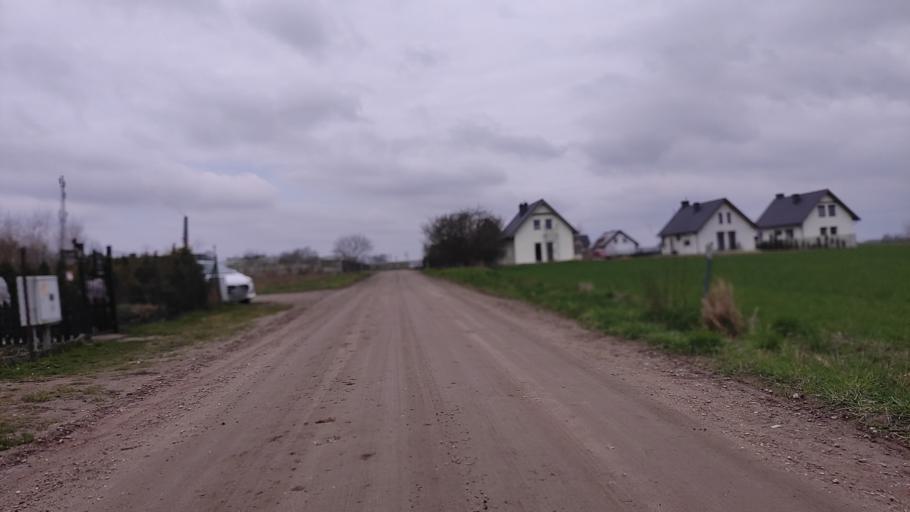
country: PL
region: Greater Poland Voivodeship
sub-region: Powiat poznanski
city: Kostrzyn
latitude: 52.4045
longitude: 17.1681
